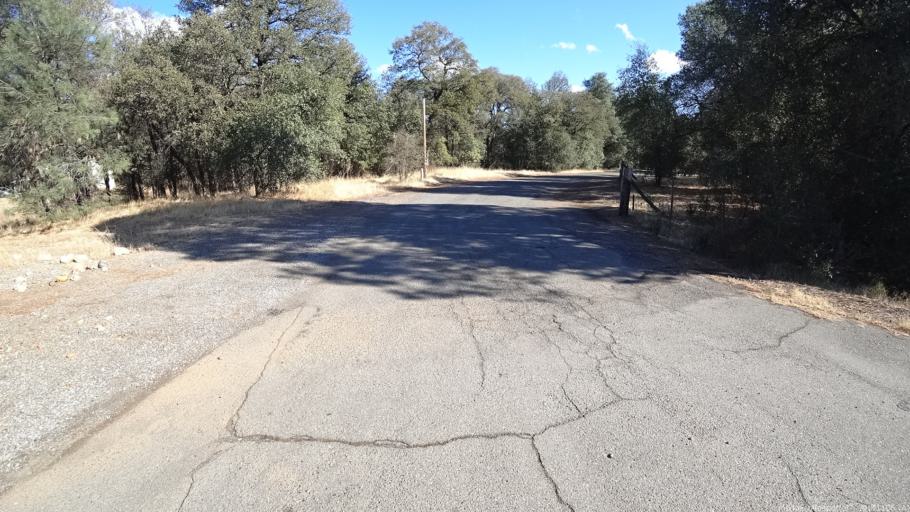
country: US
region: California
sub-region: Shasta County
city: Redding
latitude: 40.6096
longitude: -122.3162
